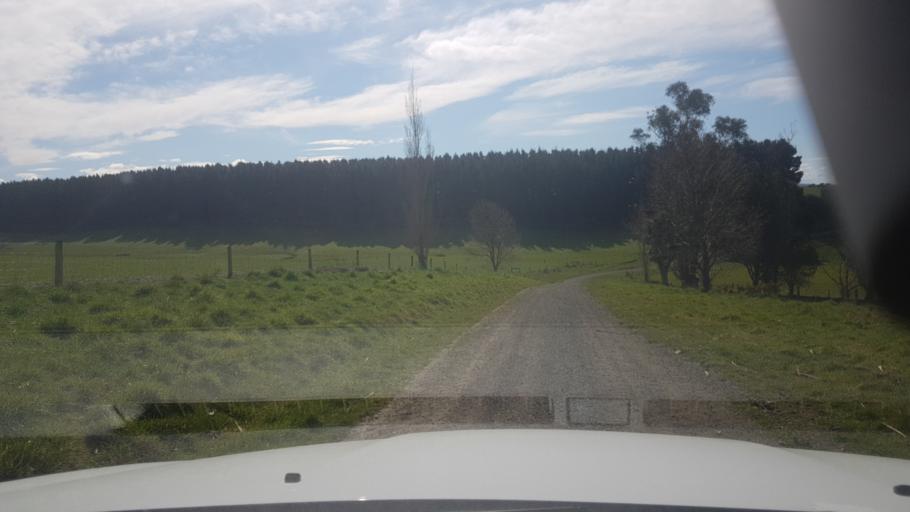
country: NZ
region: Canterbury
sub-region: Timaru District
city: Pleasant Point
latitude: -44.1979
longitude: 171.1875
